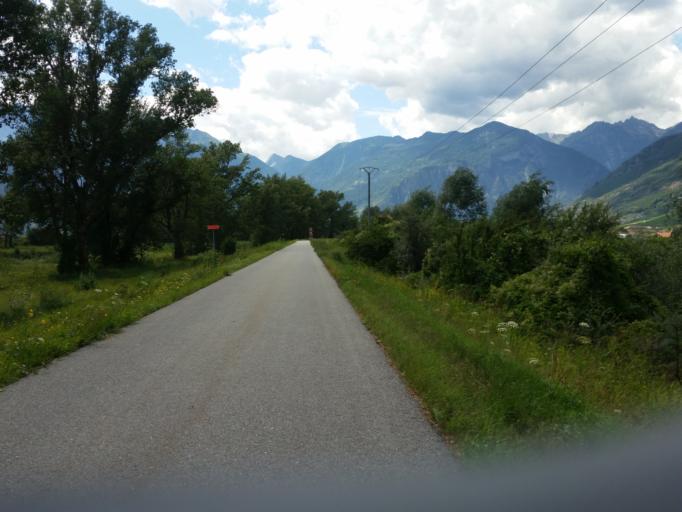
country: CH
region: Valais
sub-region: Martigny District
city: Fully
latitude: 46.1397
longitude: 7.1324
